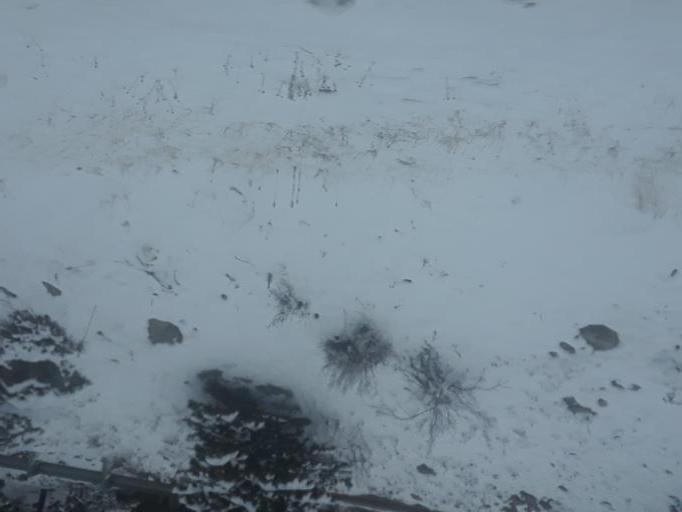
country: US
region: Colorado
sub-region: Boulder County
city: Coal Creek
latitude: 39.9228
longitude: -105.4193
